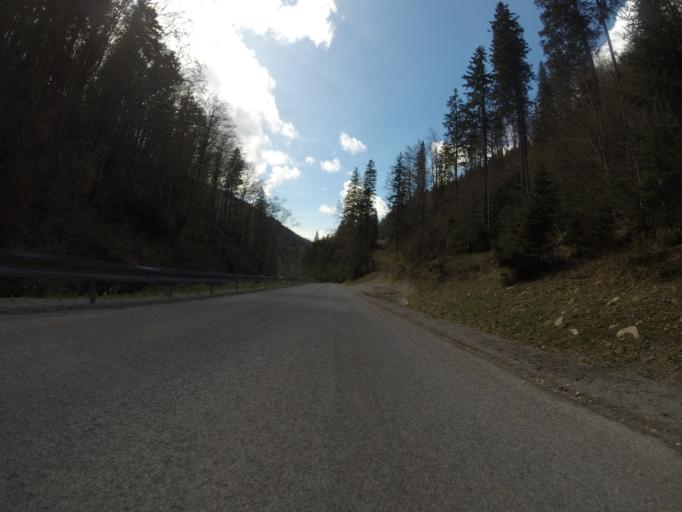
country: SK
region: Banskobystricky
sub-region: Okres Banska Bystrica
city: Brezno
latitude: 48.9199
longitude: 19.5992
